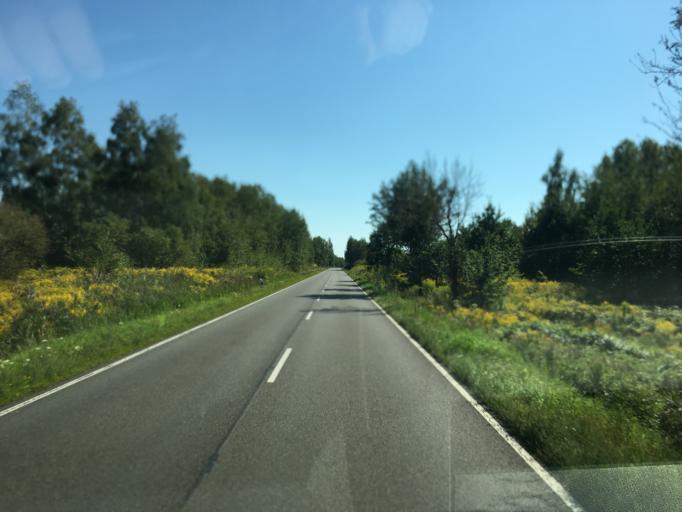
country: DE
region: Brandenburg
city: Welzow
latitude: 51.5612
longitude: 14.1219
